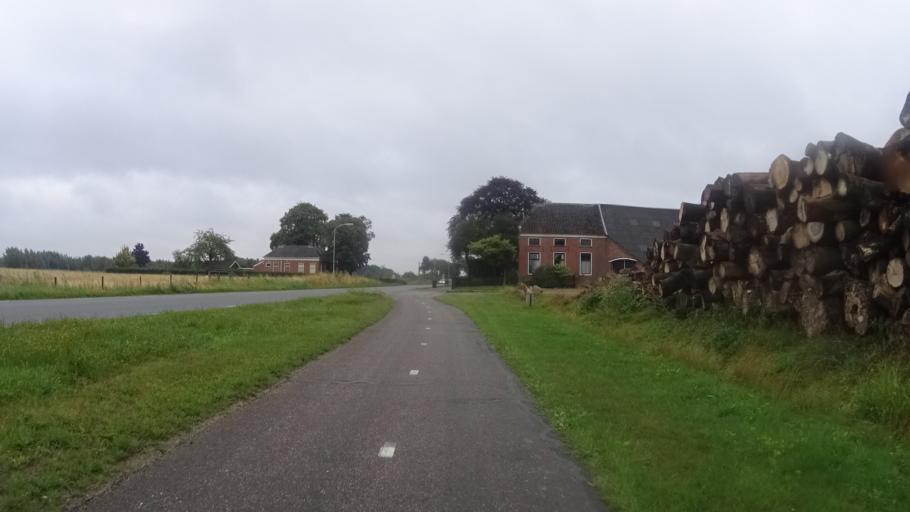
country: NL
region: Groningen
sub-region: Gemeente  Oldambt
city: Winschoten
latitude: 53.1562
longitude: 7.0594
